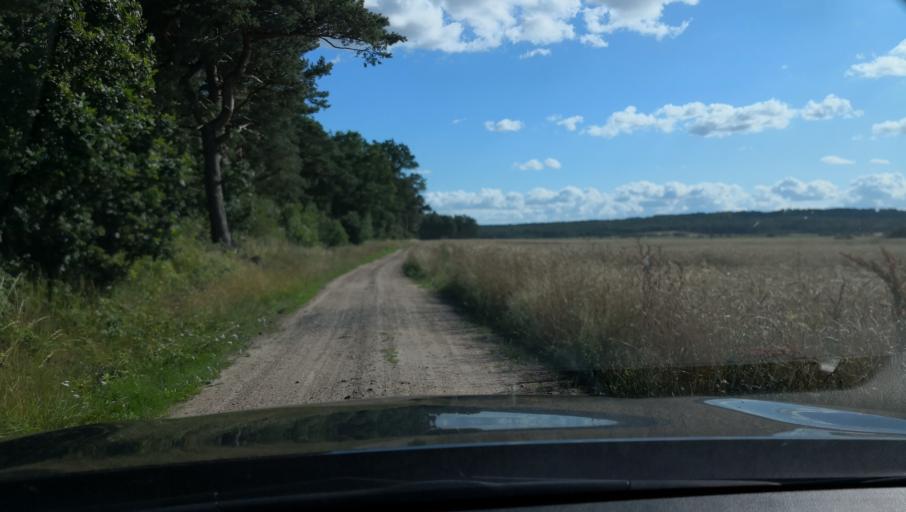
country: SE
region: Skane
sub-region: Kristianstads Kommun
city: Degeberga
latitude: 55.8028
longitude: 14.1967
